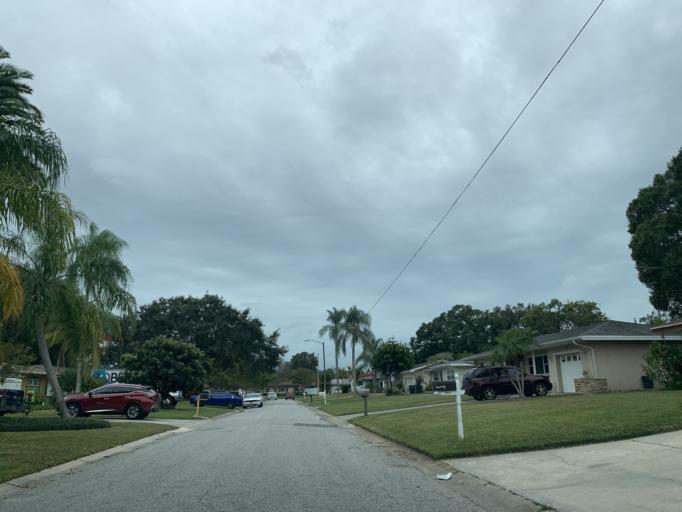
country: US
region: Florida
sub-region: Pinellas County
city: Belleair
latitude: 27.9366
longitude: -82.7813
